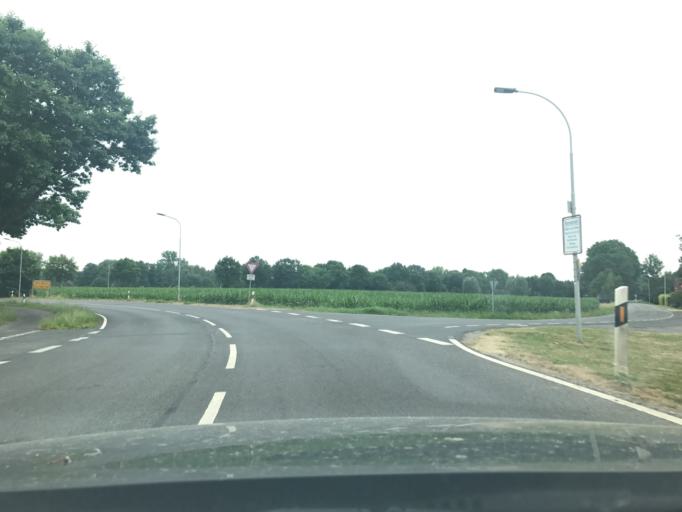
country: DE
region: North Rhine-Westphalia
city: Kempen
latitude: 51.3944
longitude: 6.4220
